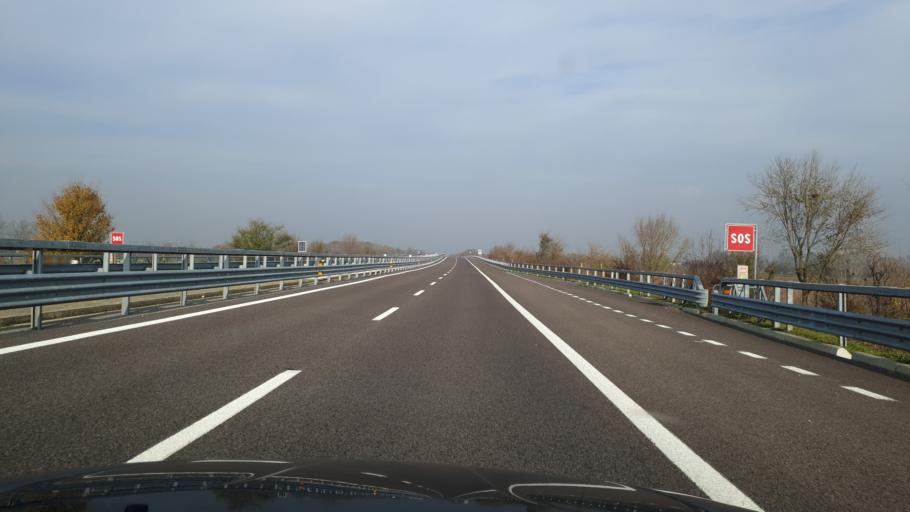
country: IT
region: Veneto
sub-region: Provincia di Padova
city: Piacenza d'Adige
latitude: 45.1584
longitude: 11.5338
